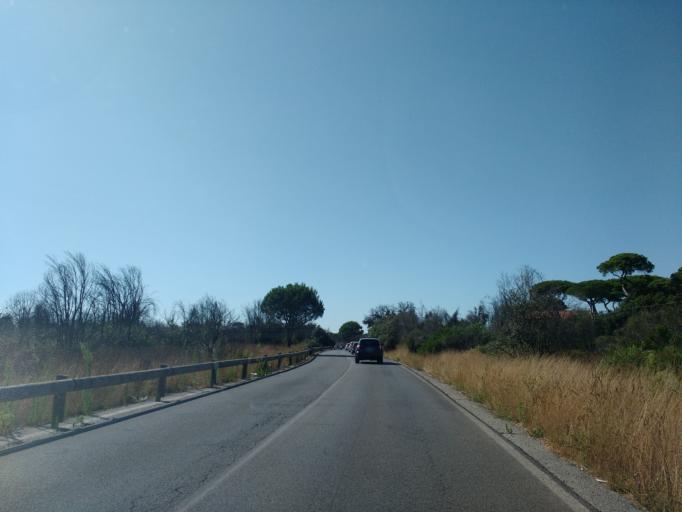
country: IT
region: Latium
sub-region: Citta metropolitana di Roma Capitale
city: Acilia-Castel Fusano-Ostia Antica
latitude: 41.7261
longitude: 12.3413
